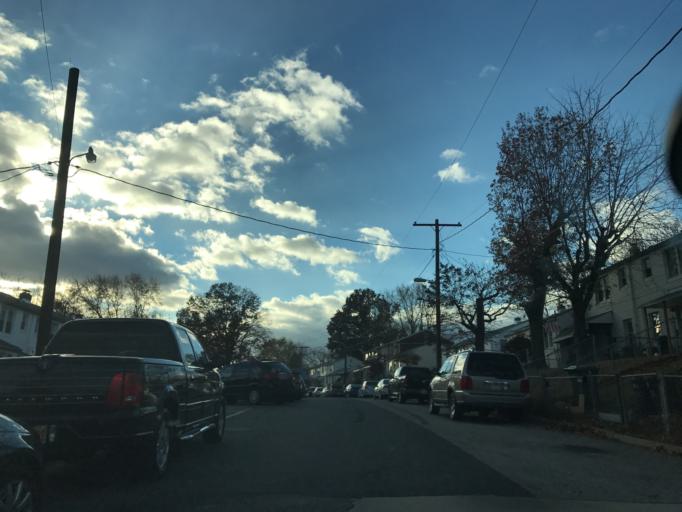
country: US
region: Maryland
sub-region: Baltimore County
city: Rosedale
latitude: 39.3109
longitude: -76.5555
